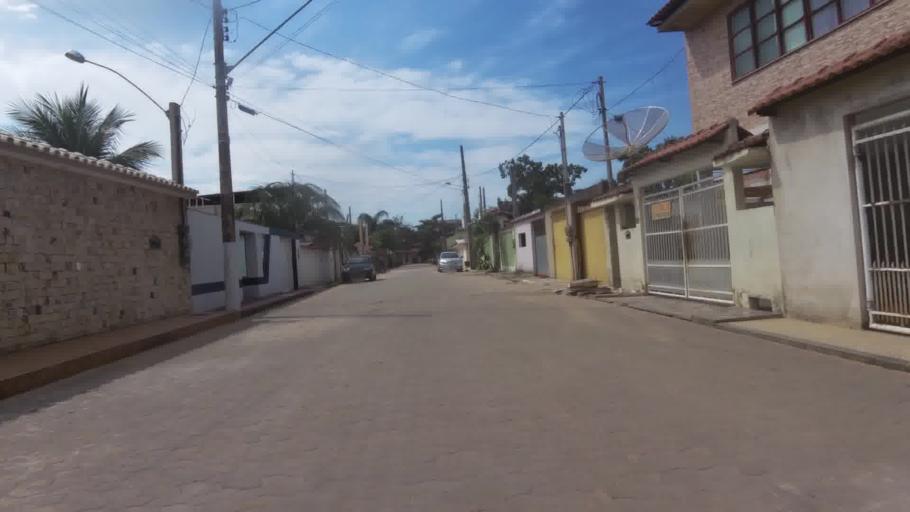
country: BR
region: Espirito Santo
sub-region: Piuma
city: Piuma
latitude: -20.8411
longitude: -40.7383
